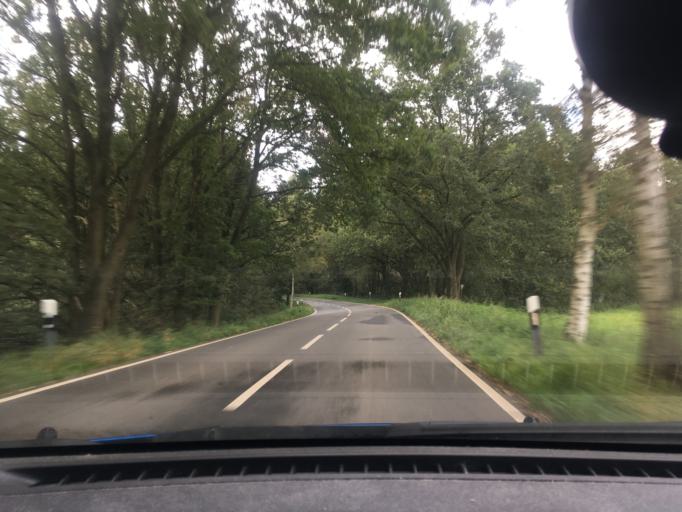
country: DE
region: Lower Saxony
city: Nahrendorf
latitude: 53.1674
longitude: 10.8337
